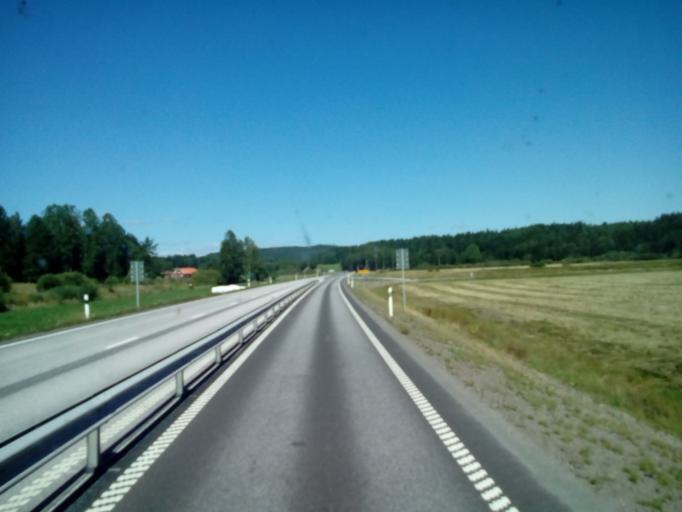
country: SE
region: OEstergoetland
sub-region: Kinda Kommun
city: Kisa
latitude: 58.0449
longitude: 15.6634
